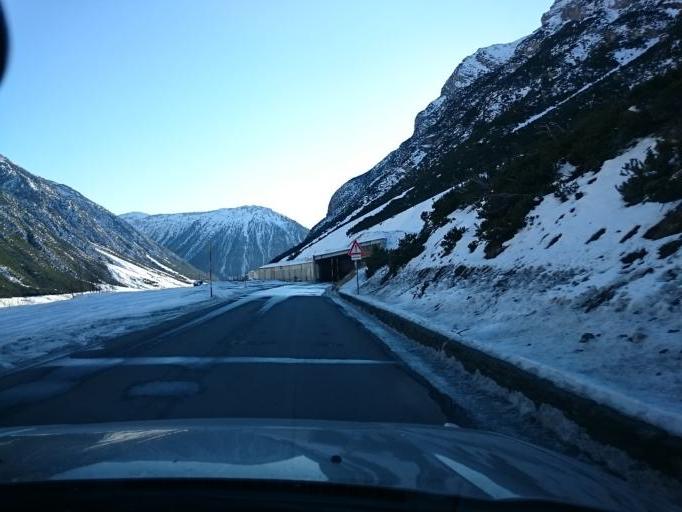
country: IT
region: Lombardy
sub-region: Provincia di Sondrio
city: Livigno
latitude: 46.5886
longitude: 10.1701
